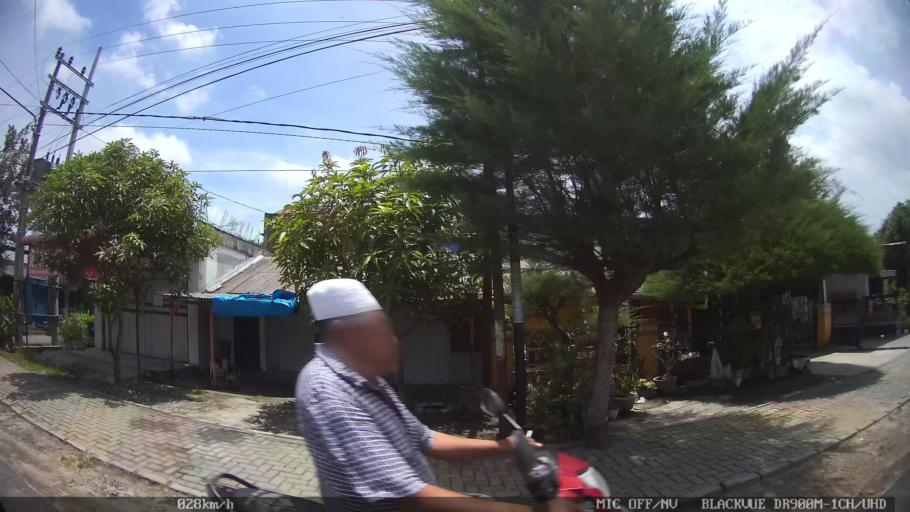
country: ID
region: North Sumatra
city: Percut
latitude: 3.5442
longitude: 98.8743
